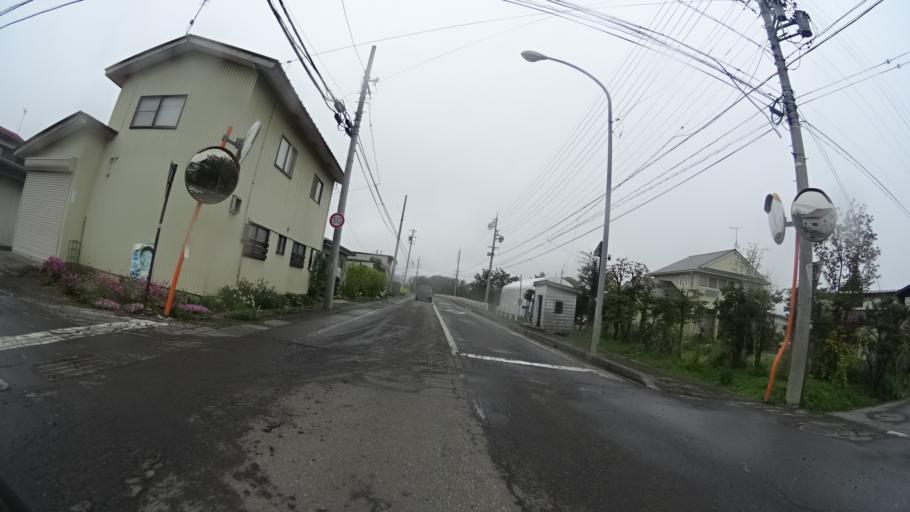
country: JP
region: Nagano
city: Nagano-shi
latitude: 36.7793
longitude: 138.2003
